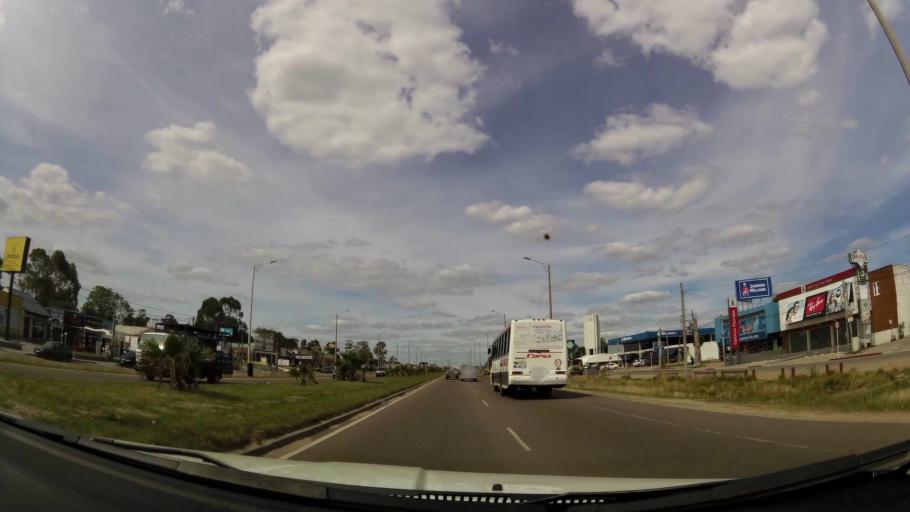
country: UY
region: Canelones
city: Barra de Carrasco
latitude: -34.8335
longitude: -55.9795
